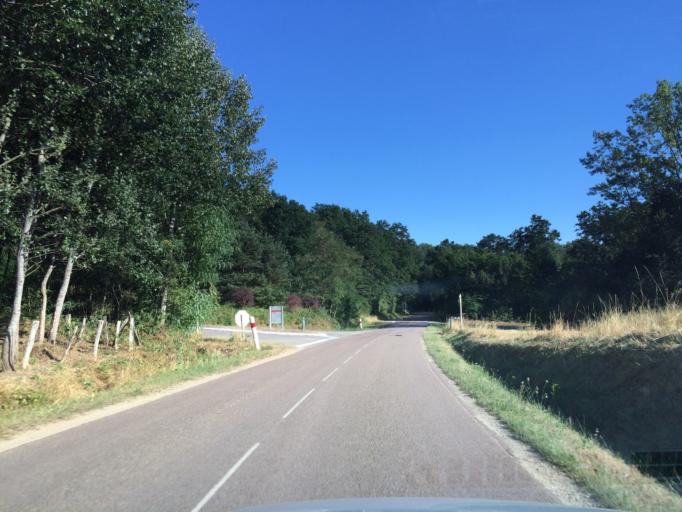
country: FR
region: Bourgogne
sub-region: Departement de l'Yonne
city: Fleury-la-Vallee
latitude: 47.8876
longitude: 3.4365
